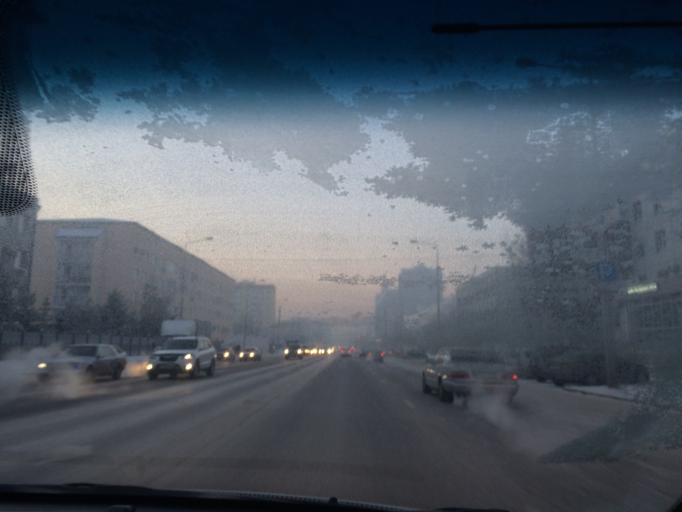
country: KZ
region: Astana Qalasy
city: Astana
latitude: 51.1731
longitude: 71.4066
